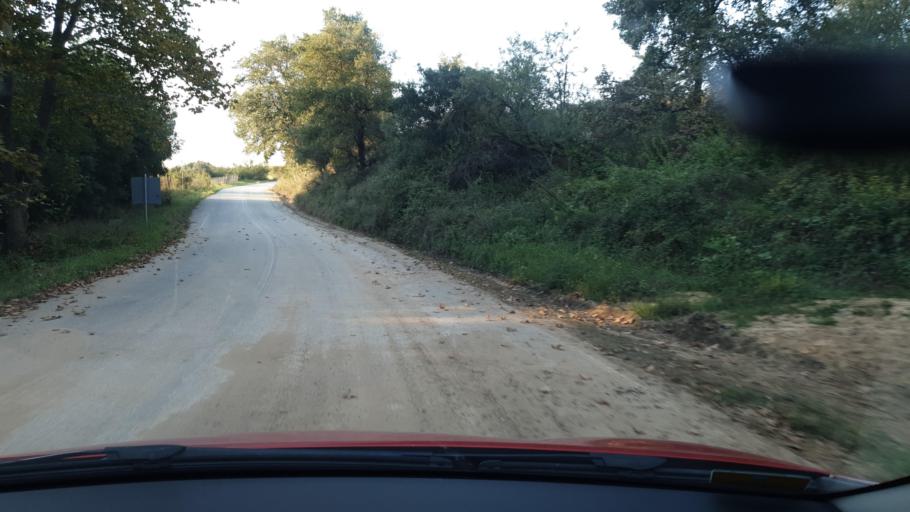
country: GR
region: Central Macedonia
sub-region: Nomos Thessalonikis
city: Nea Apollonia
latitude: 40.5536
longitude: 23.4316
